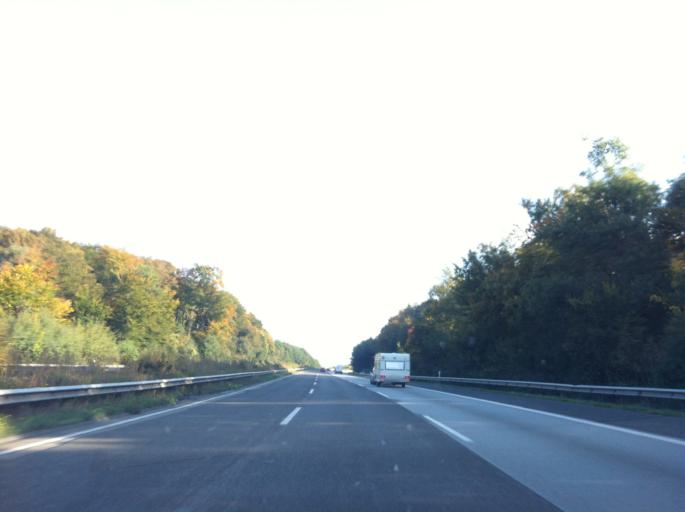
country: DE
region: Rheinland-Pfalz
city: Ebernhahn
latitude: 50.4812
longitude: 7.7561
